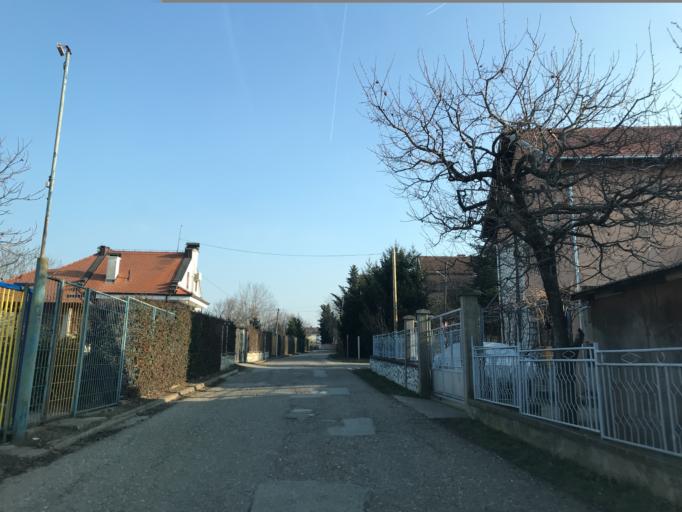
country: RS
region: Autonomna Pokrajina Vojvodina
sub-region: Juznobacki Okrug
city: Novi Sad
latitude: 45.2270
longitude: 19.8533
